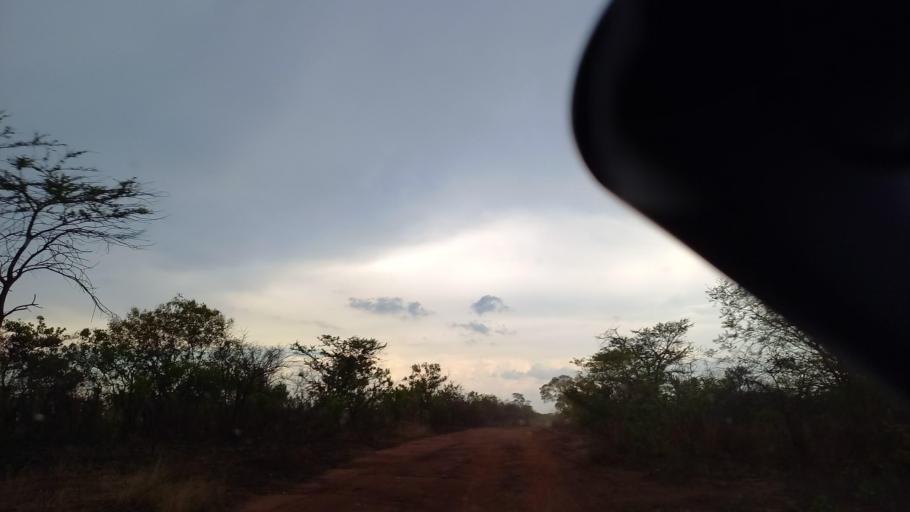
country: ZM
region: Lusaka
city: Kafue
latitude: -15.9967
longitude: 28.2770
